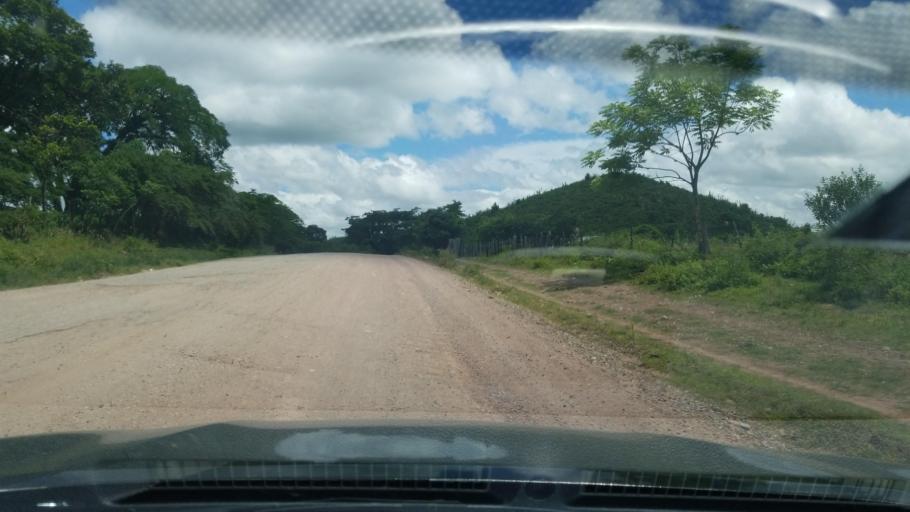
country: HN
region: Francisco Morazan
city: Talanga
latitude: 14.3571
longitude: -87.0461
